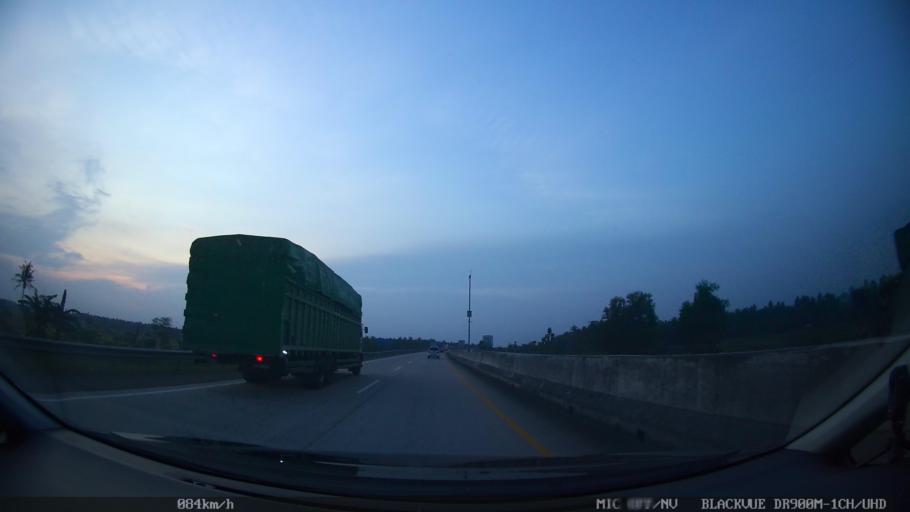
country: ID
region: Lampung
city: Kalianda
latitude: -5.6615
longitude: 105.5975
